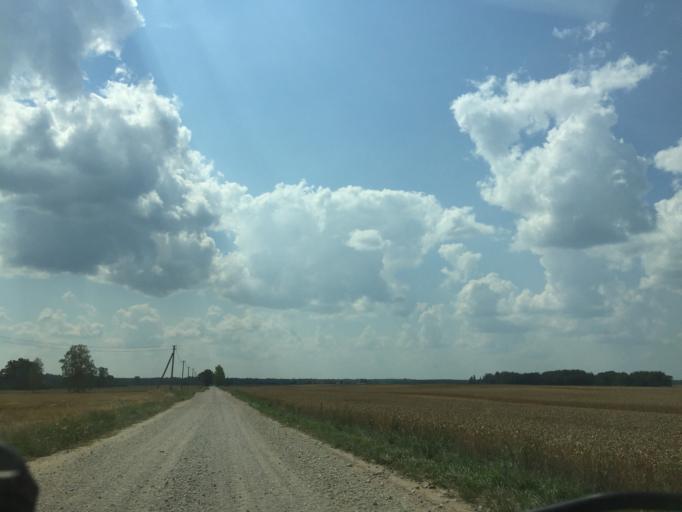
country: LT
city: Zagare
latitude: 56.3897
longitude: 23.1924
